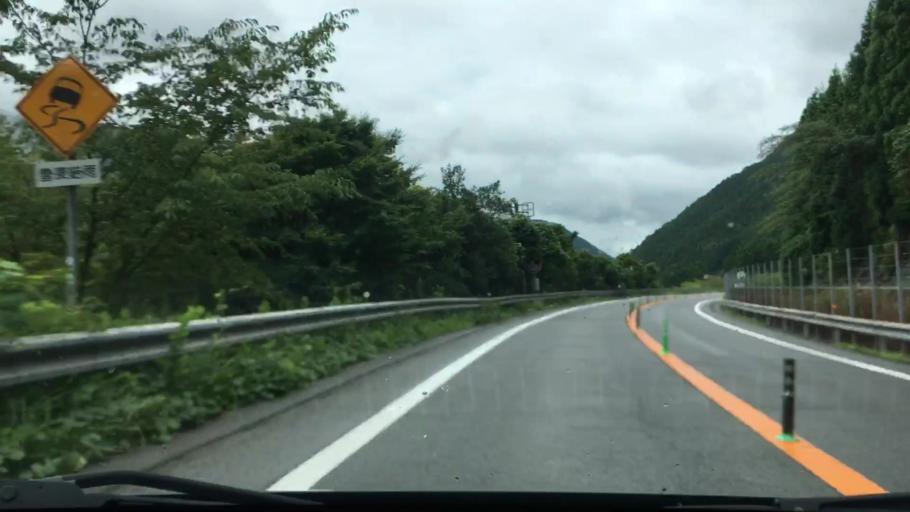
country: JP
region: Hyogo
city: Nishiwaki
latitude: 35.1376
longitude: 134.7901
